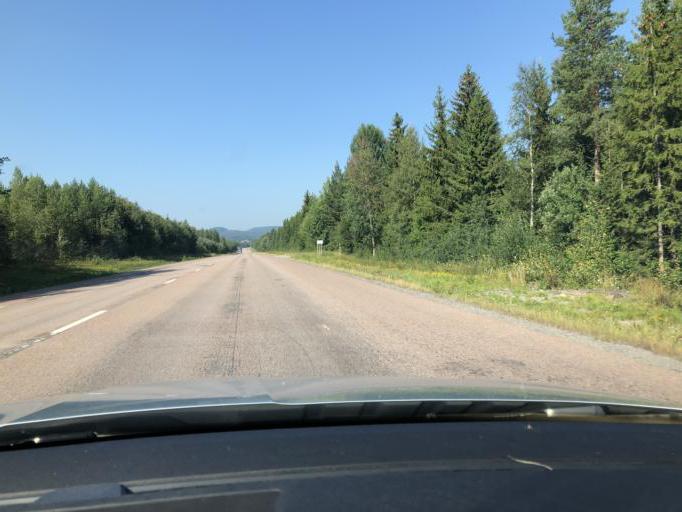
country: SE
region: Vaesternorrland
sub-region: OErnskoeldsviks Kommun
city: Bjasta
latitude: 63.2958
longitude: 18.5452
